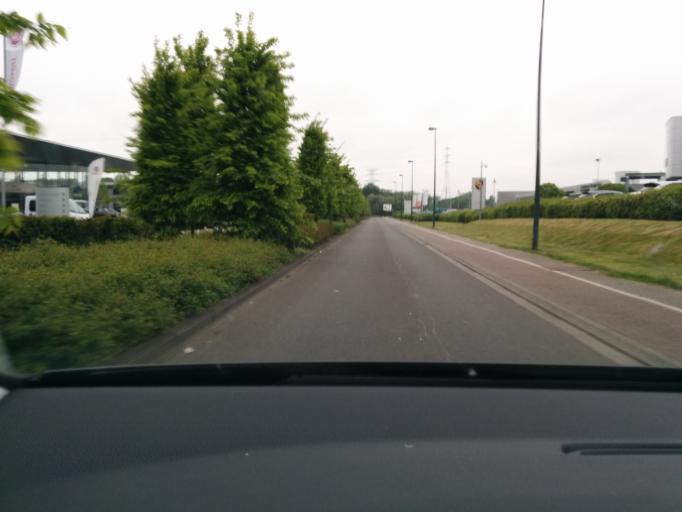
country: BE
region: Flanders
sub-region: Provincie Vlaams-Brabant
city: Drogenbos
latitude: 50.7904
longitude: 4.3100
